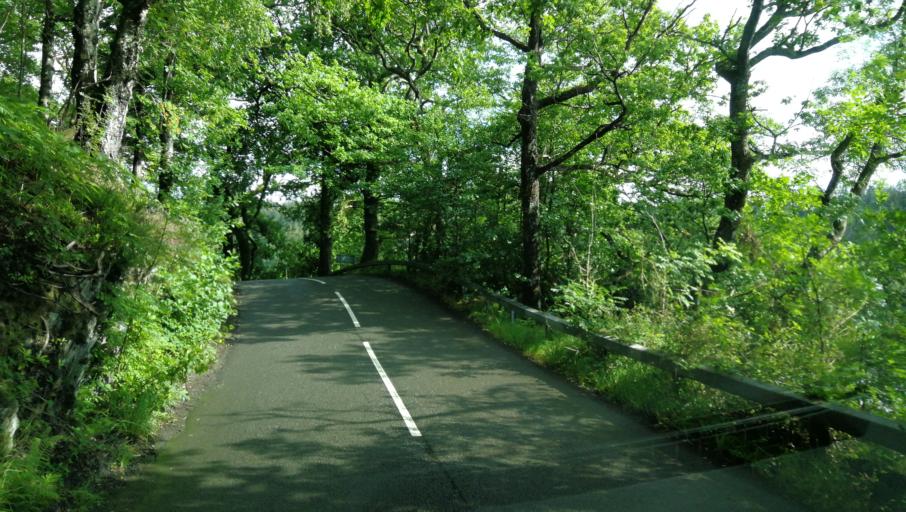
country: GB
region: Scotland
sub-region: Stirling
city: Balfron
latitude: 56.2278
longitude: -4.3900
